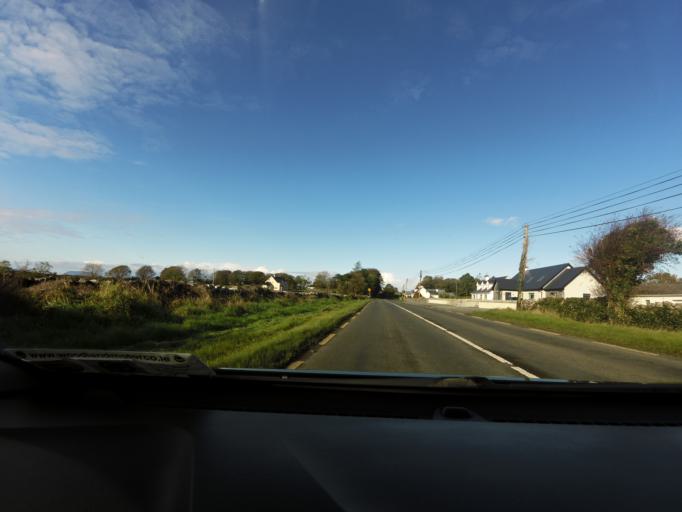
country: IE
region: Connaught
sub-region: Maigh Eo
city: Ballinrobe
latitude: 53.5411
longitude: -9.0975
